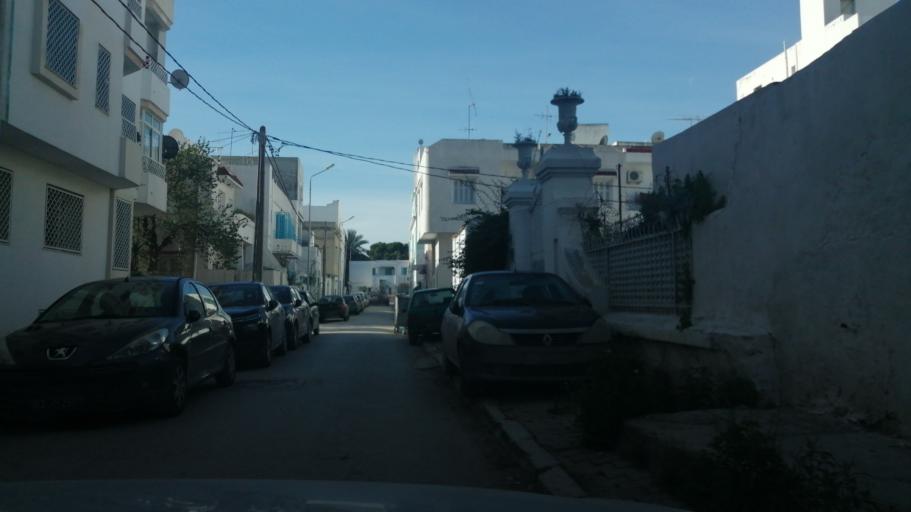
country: TN
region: Tunis
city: Tunis
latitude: 36.8125
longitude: 10.1717
